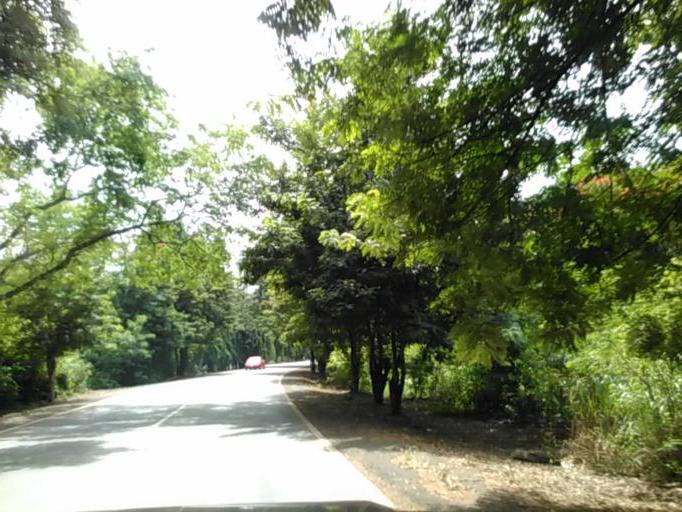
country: GH
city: Akropong
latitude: 6.2660
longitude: 0.0650
